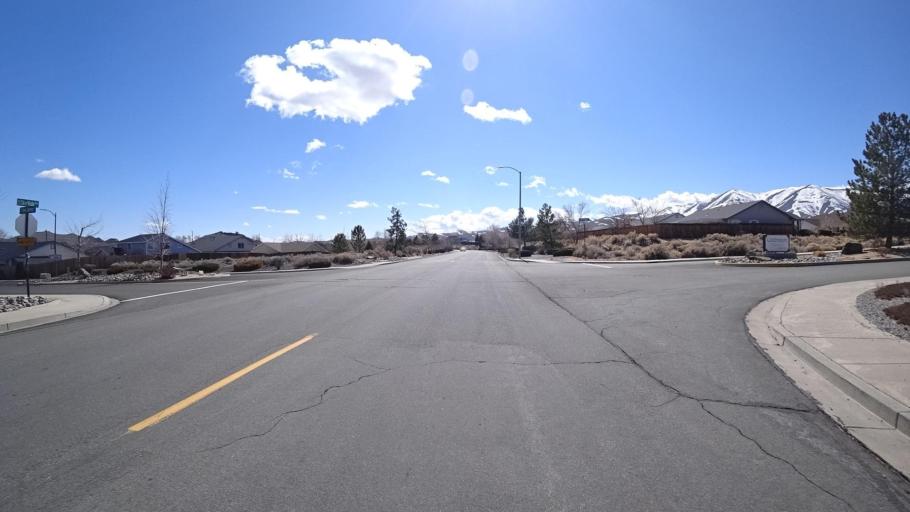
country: US
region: Nevada
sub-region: Washoe County
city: Lemmon Valley
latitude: 39.6387
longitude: -119.8676
